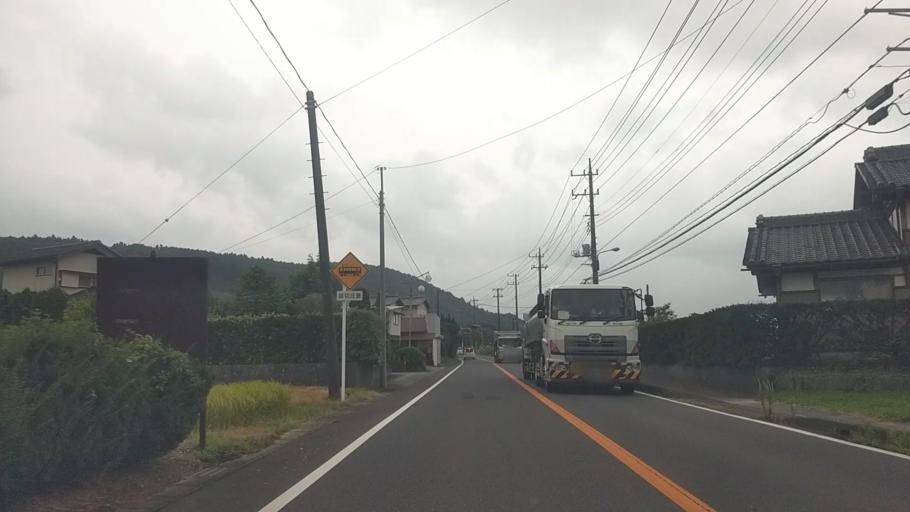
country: JP
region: Chiba
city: Kisarazu
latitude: 35.3078
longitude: 140.0676
